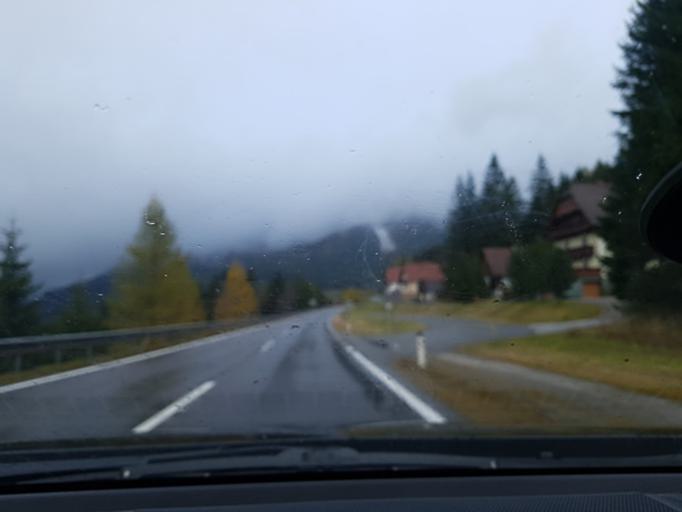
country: AT
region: Styria
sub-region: Politischer Bezirk Murtal
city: Hohentauern
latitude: 47.4285
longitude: 14.4652
